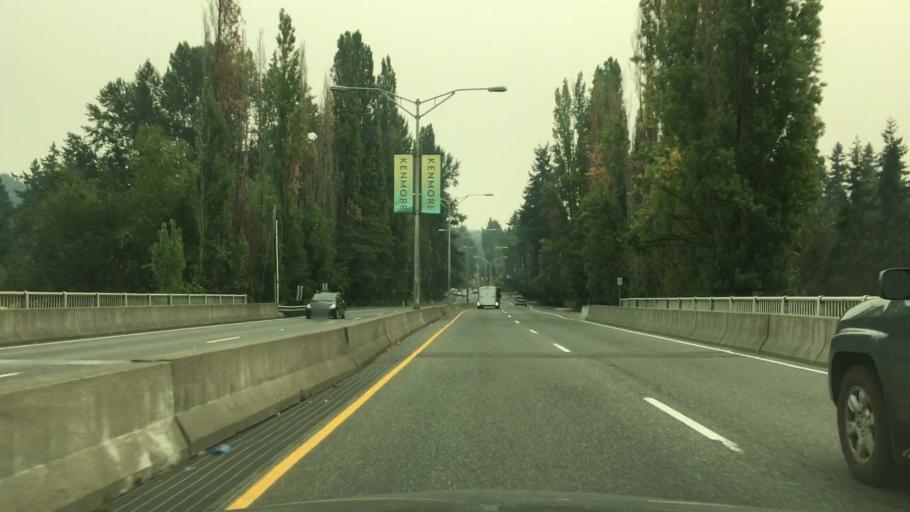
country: US
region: Washington
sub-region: King County
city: Kenmore
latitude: 47.7544
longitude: -122.2499
